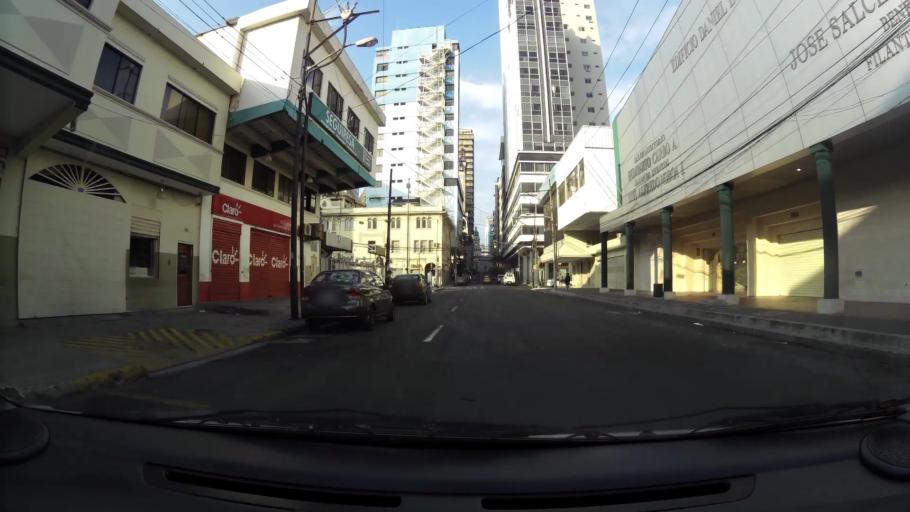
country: EC
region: Guayas
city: Eloy Alfaro
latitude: -2.1892
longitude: -79.8809
